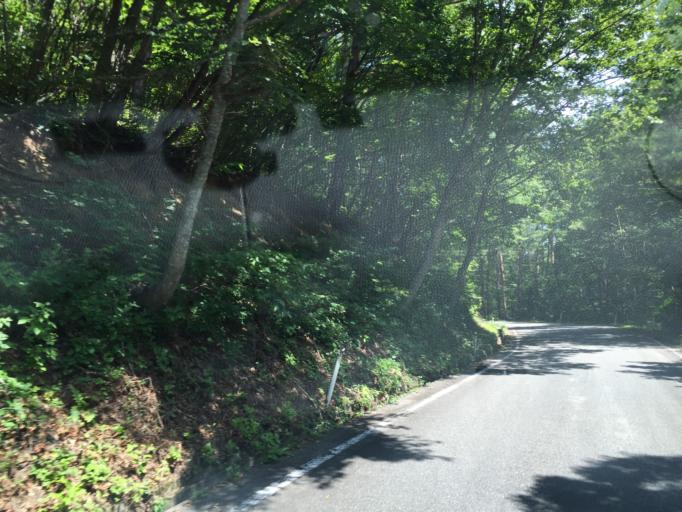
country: JP
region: Fukushima
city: Inawashiro
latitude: 37.4725
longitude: 140.0425
